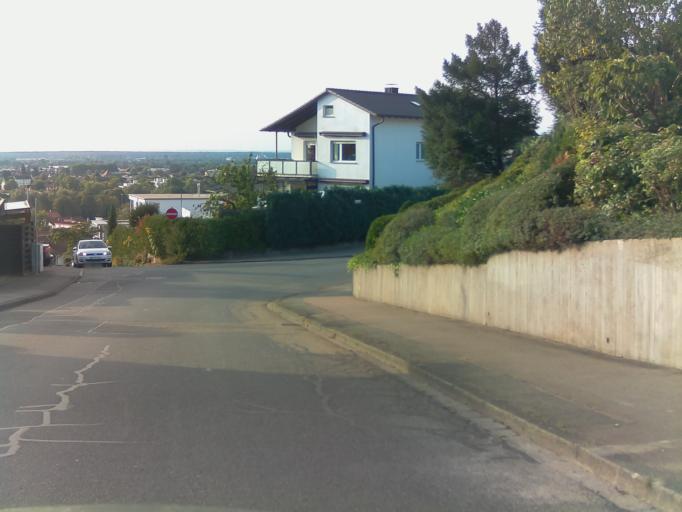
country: DE
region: Baden-Wuerttemberg
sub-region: Karlsruhe Region
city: Weinheim
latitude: 49.5380
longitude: 8.6636
